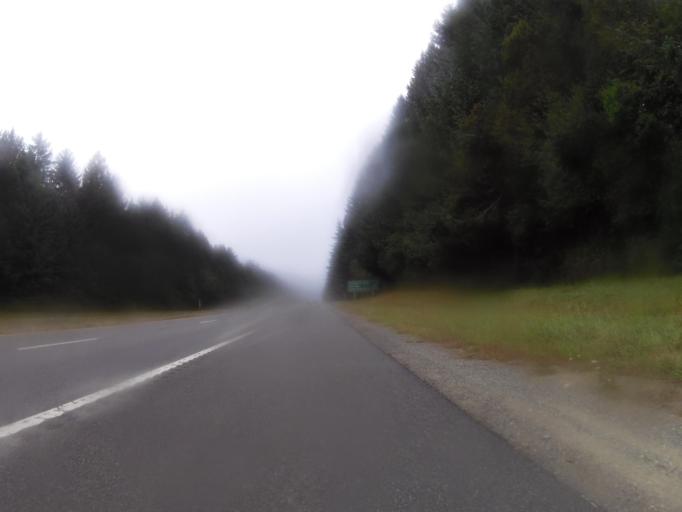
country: US
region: California
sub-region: Del Norte County
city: Bertsch-Oceanview
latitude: 41.7925
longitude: -124.1614
